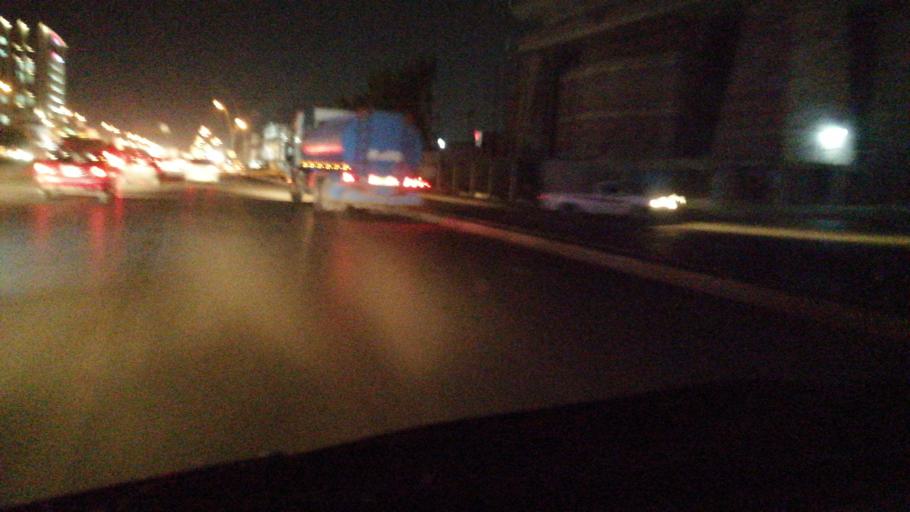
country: IQ
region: Arbil
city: Erbil
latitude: 36.1574
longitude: 43.9859
